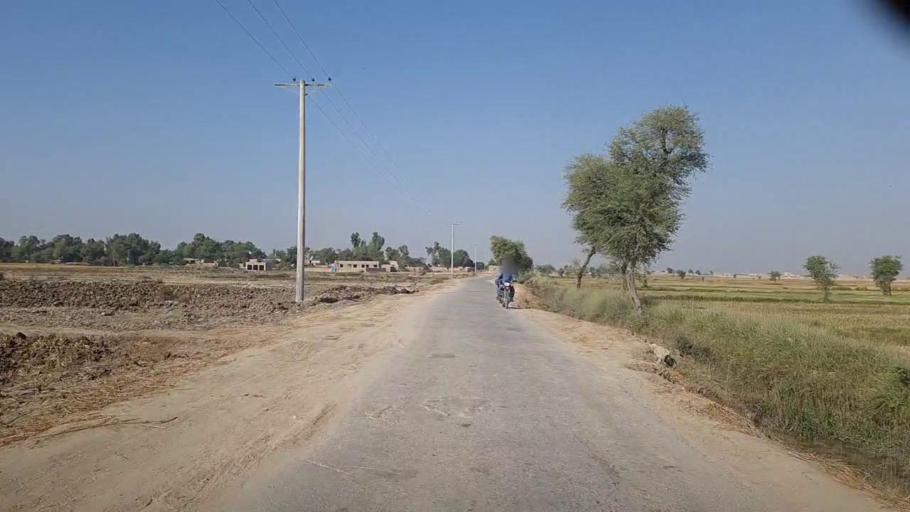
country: PK
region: Sindh
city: Tangwani
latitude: 28.2522
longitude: 68.9958
